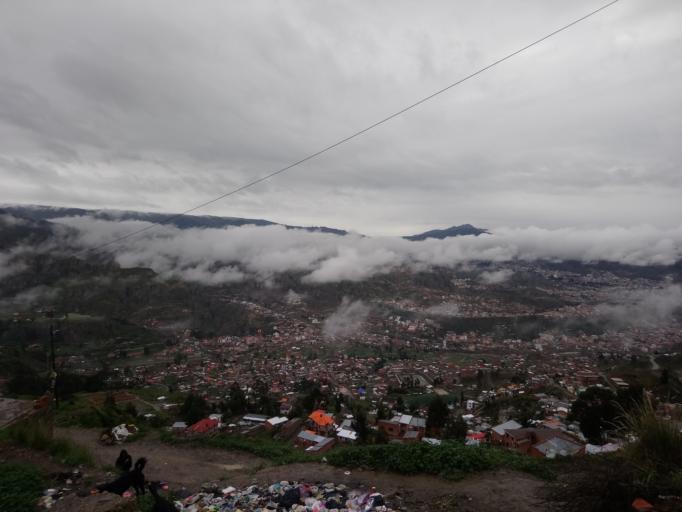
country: BO
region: La Paz
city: La Paz
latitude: -16.4954
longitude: -68.1000
